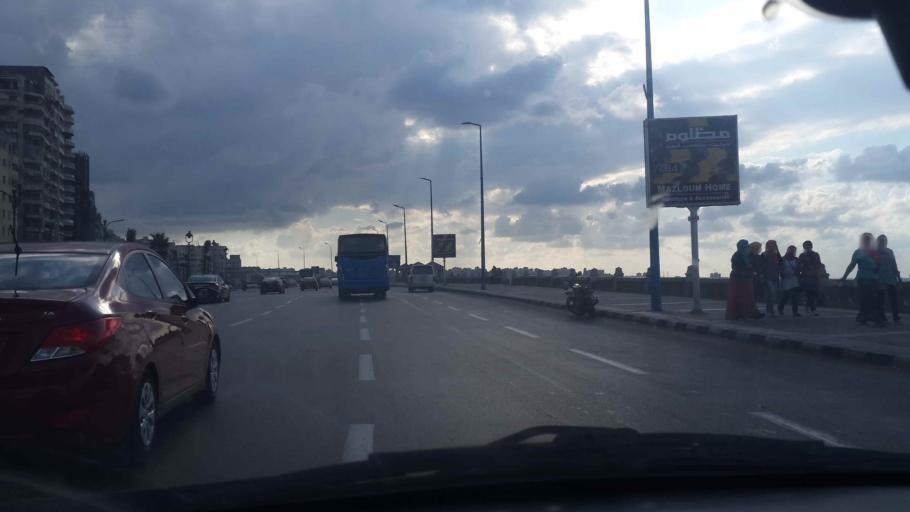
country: EG
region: Alexandria
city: Alexandria
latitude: 31.2148
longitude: 29.9206
